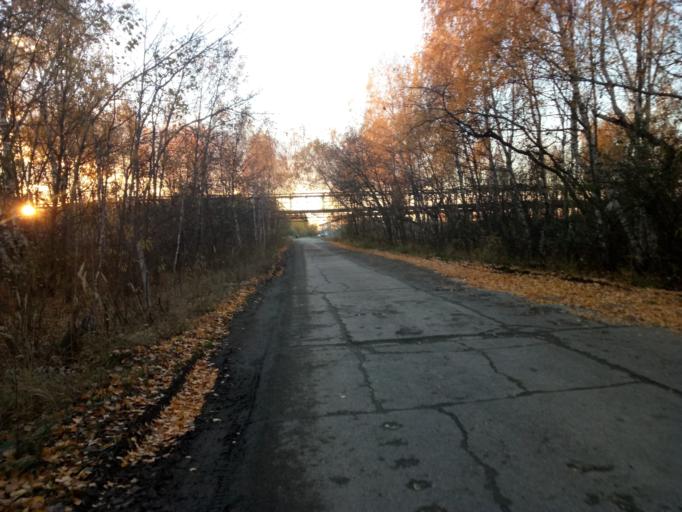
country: RU
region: Tatarstan
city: Staroye Arakchino
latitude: 55.8820
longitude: 48.9708
